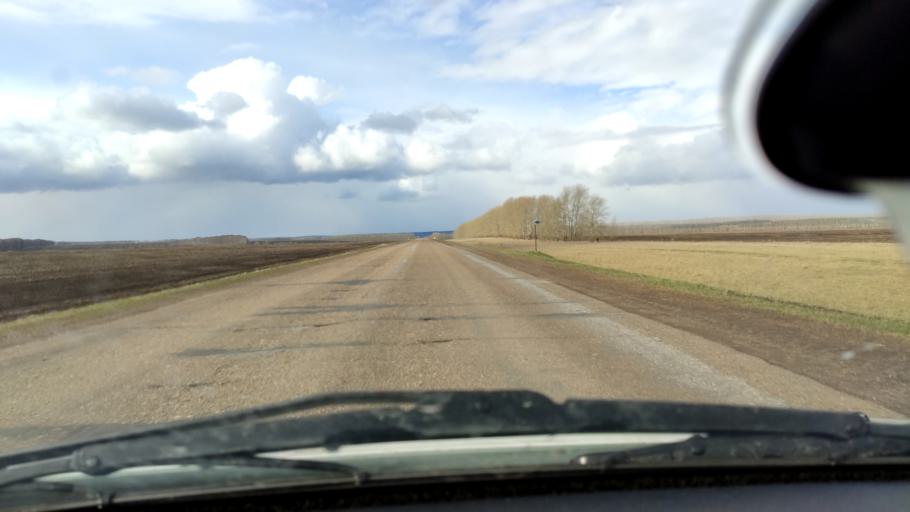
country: RU
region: Bashkortostan
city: Buzdyak
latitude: 54.7318
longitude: 54.5670
